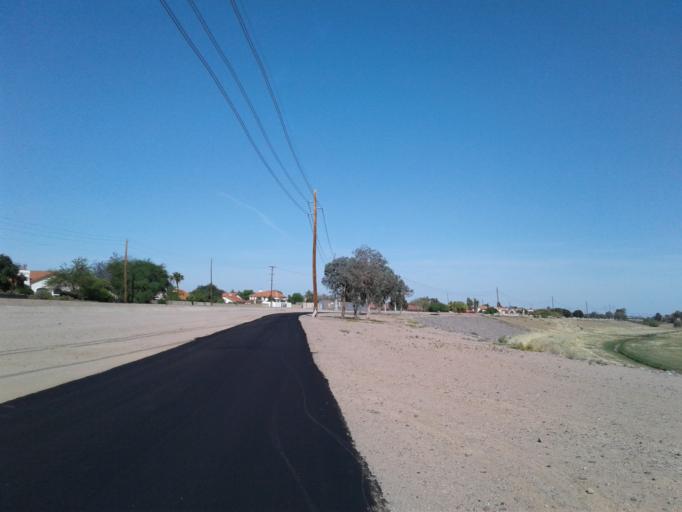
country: US
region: Arizona
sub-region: Maricopa County
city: Glendale
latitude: 33.5986
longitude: -112.1740
